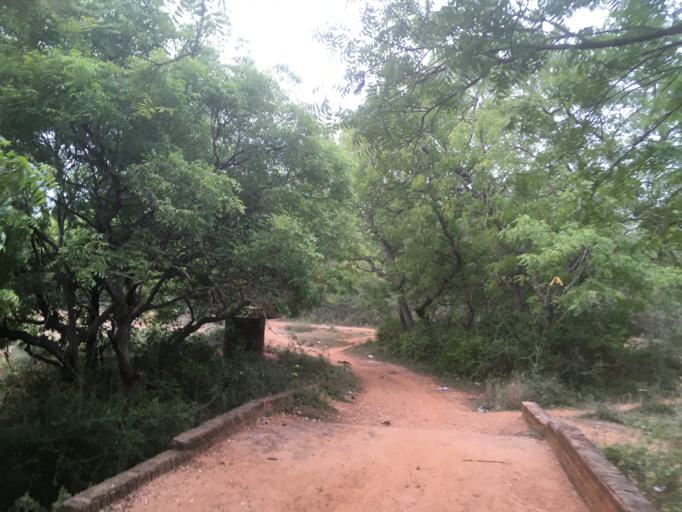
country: IN
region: Tamil Nadu
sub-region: Villupuram
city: Auroville
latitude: 12.0096
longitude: 79.8041
